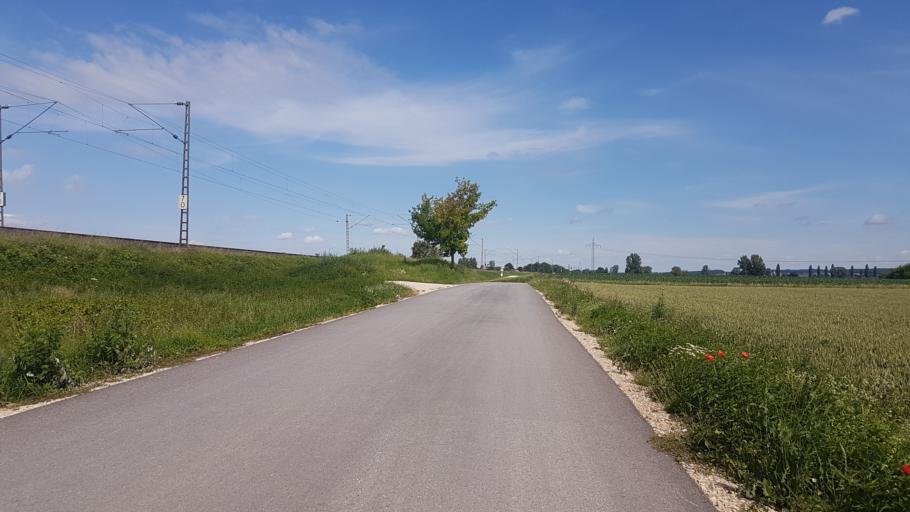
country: DE
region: Bavaria
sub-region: Regierungsbezirk Mittelfranken
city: Markt Berolzheim
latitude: 49.0081
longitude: 10.8589
